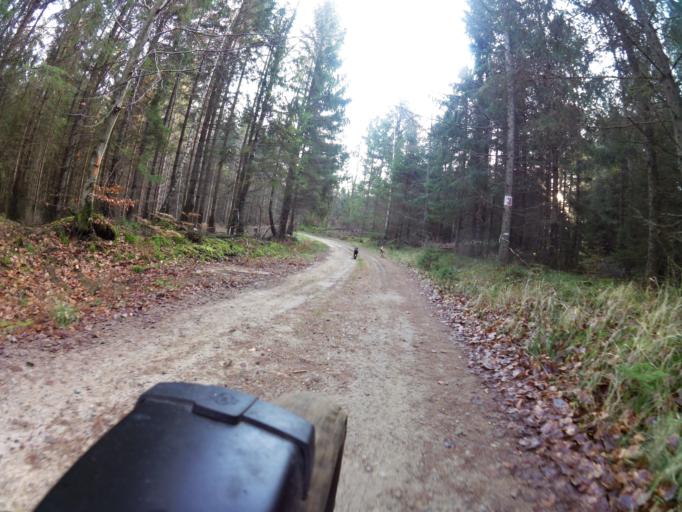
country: PL
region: West Pomeranian Voivodeship
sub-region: Powiat koszalinski
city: Polanow
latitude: 54.1773
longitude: 16.7225
